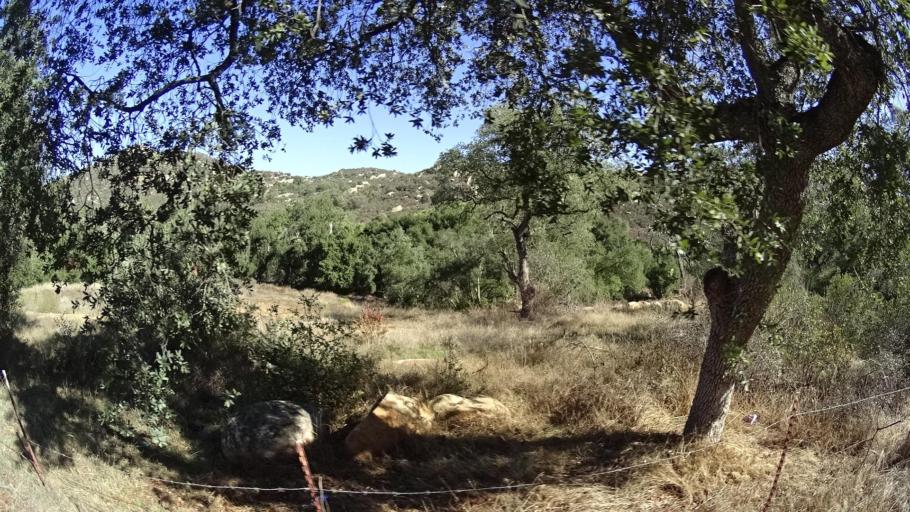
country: US
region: California
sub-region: San Diego County
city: Jamul
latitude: 32.7151
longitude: -116.7637
